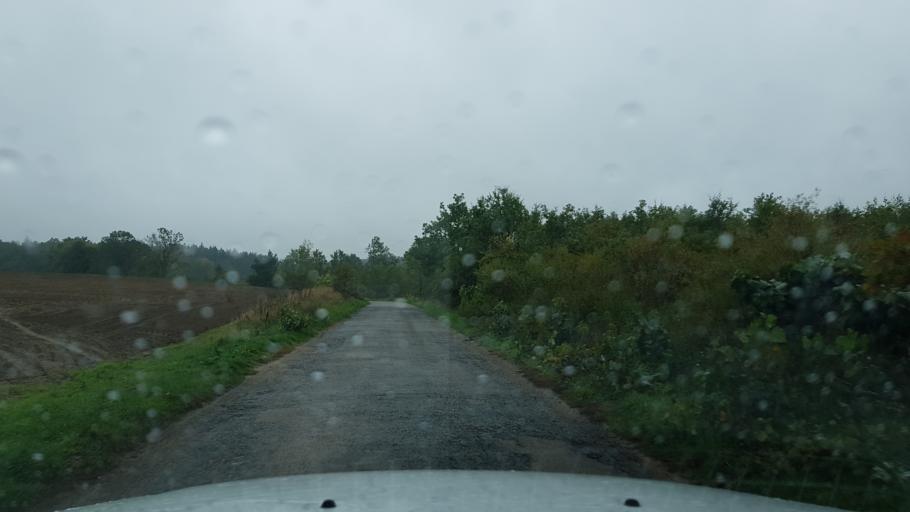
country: PL
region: West Pomeranian Voivodeship
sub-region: Powiat mysliborski
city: Barlinek
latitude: 53.0396
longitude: 15.2398
